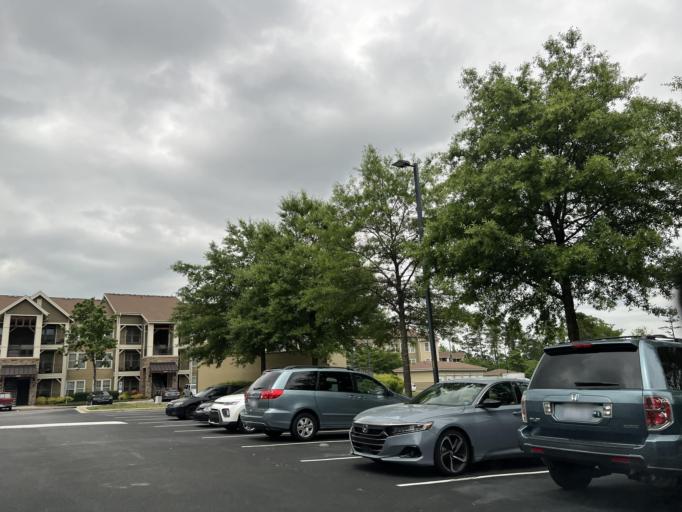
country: US
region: North Carolina
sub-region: Wake County
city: Raleigh
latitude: 35.8744
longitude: -78.5857
